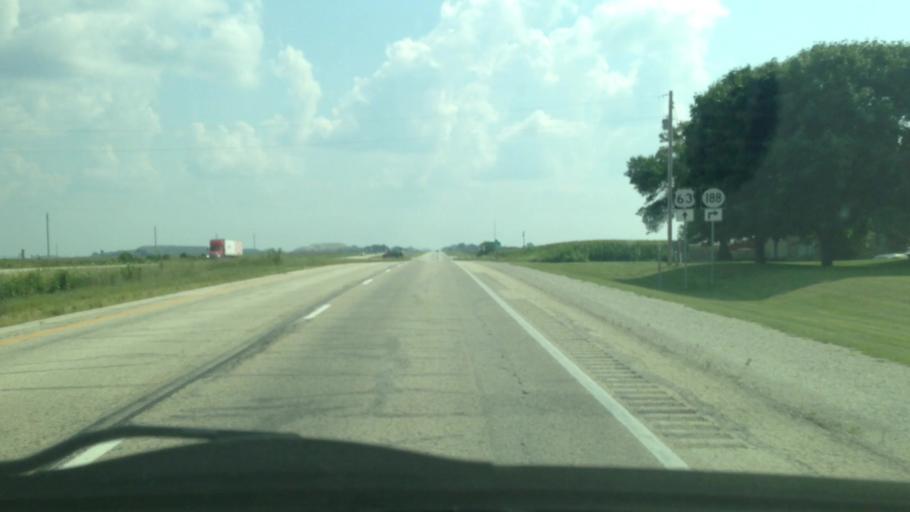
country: US
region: Iowa
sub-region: Bremer County
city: Tripoli
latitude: 42.8512
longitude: -92.3376
